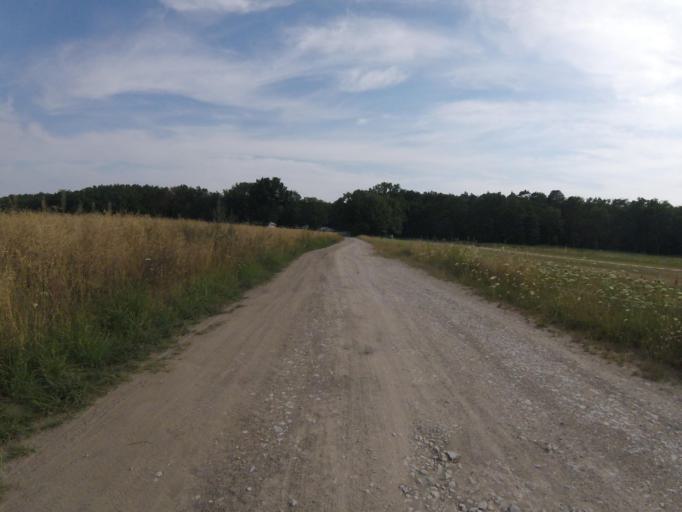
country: DE
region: Brandenburg
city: Spreenhagen
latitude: 52.2788
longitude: 13.8104
